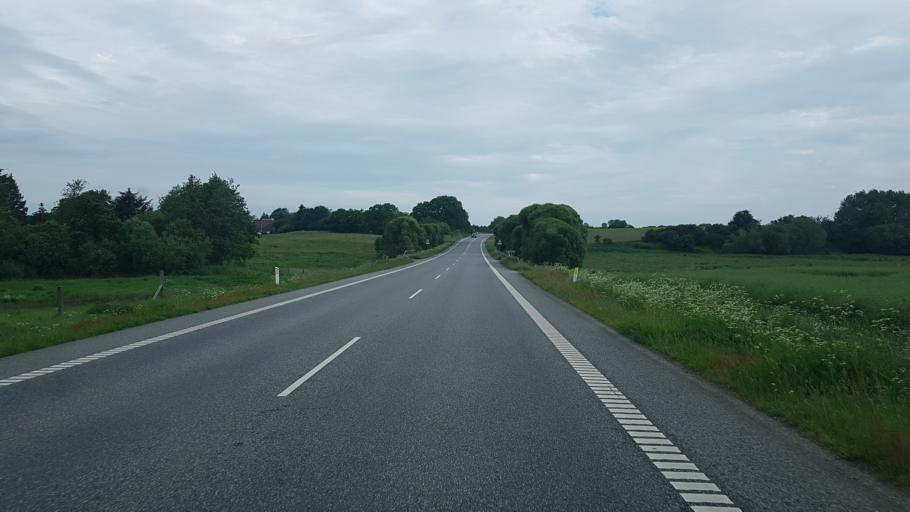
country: DK
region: South Denmark
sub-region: Vejen Kommune
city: Rodding
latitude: 55.3885
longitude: 9.0449
